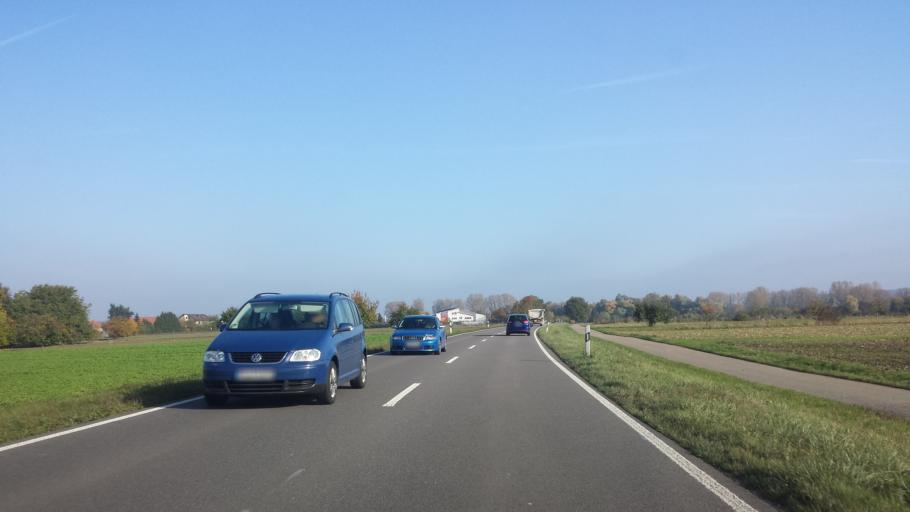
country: DE
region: Baden-Wuerttemberg
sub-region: Karlsruhe Region
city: Ubstadt-Weiher
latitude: 49.1735
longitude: 8.6239
